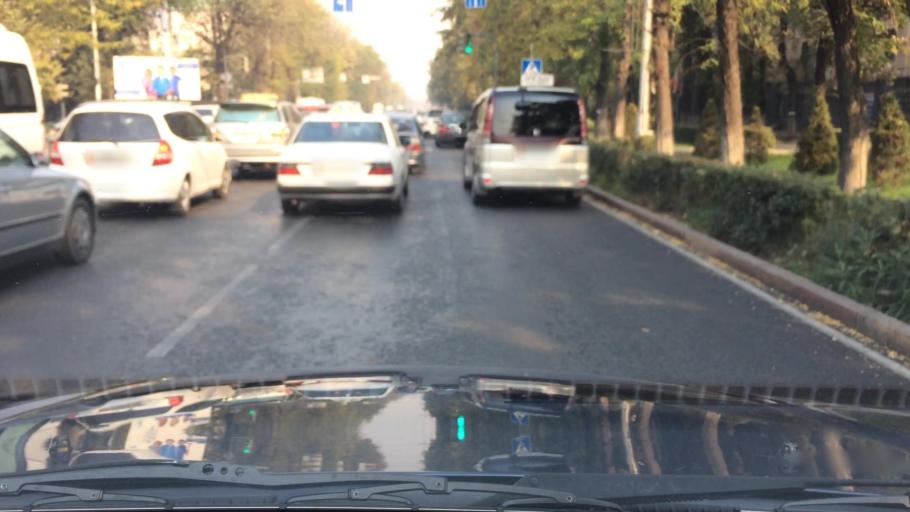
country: KG
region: Chuy
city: Bishkek
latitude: 42.8505
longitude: 74.5865
